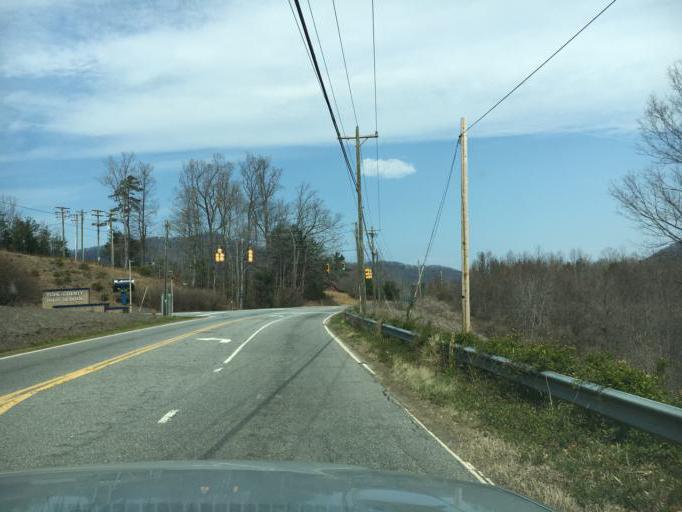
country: US
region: North Carolina
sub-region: Polk County
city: Columbus
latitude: 35.2647
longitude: -82.1830
